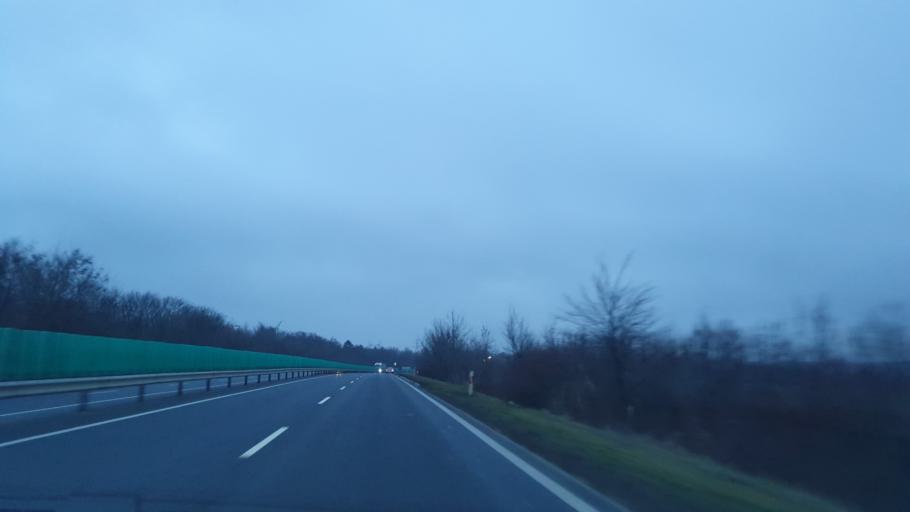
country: HU
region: Fejer
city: Kincsesbanya
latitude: 47.2111
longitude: 18.2892
